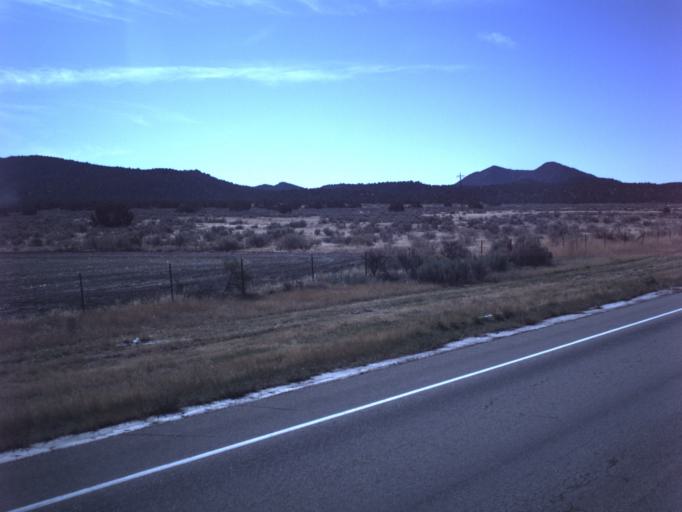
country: US
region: Utah
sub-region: Juab County
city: Nephi
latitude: 39.4586
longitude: -111.9044
